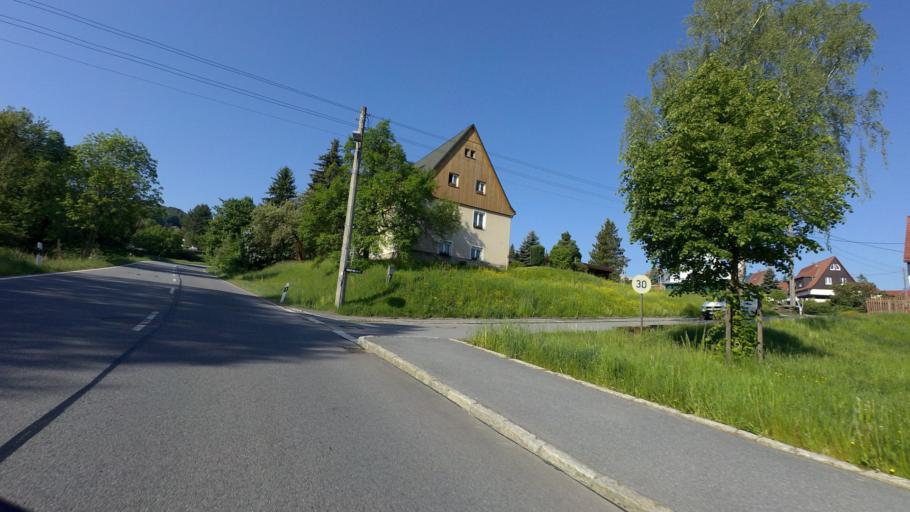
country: DE
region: Saxony
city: Sebnitz
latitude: 50.9666
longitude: 14.2536
